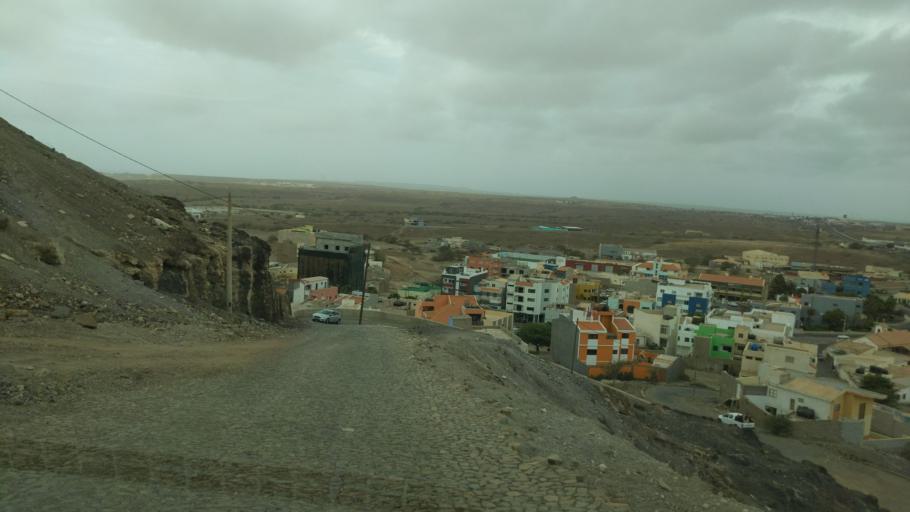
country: CV
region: Sal
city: Espargos
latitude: 16.7568
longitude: -22.9431
